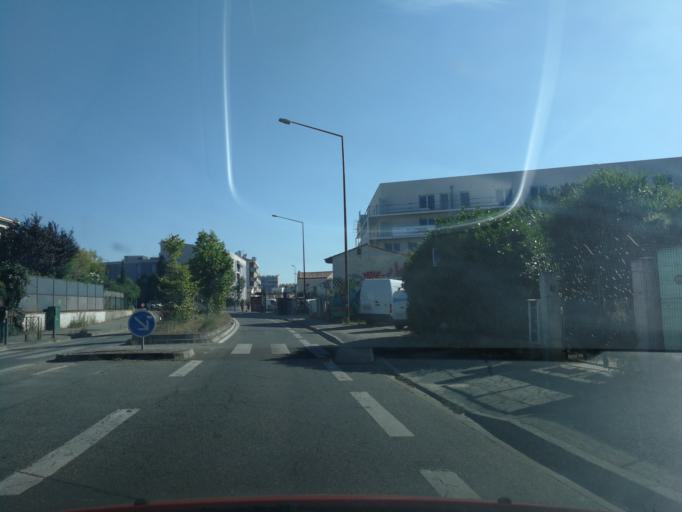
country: FR
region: Midi-Pyrenees
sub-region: Departement de la Haute-Garonne
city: Toulouse
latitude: 43.6241
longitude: 1.4544
